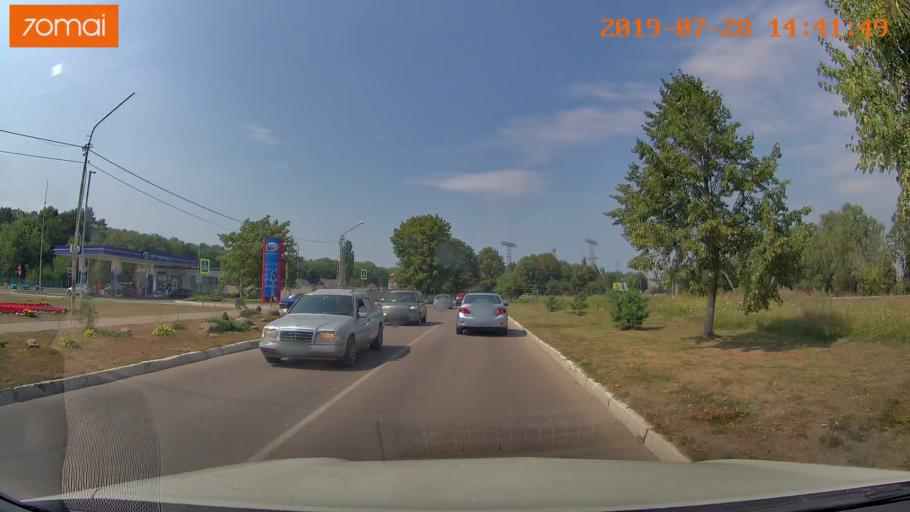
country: RU
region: Kaliningrad
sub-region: Gorod Kaliningrad
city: Yantarnyy
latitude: 54.8570
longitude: 19.9452
